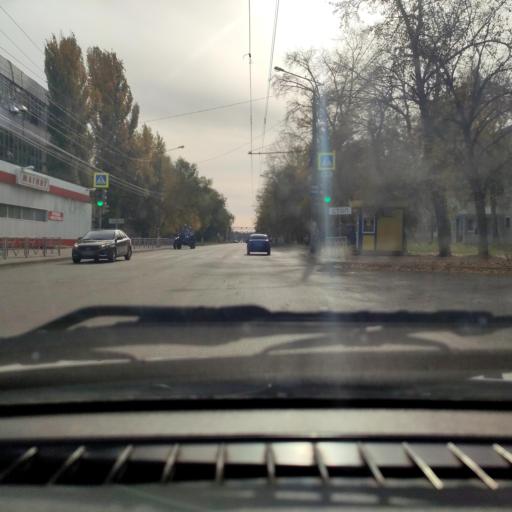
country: RU
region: Samara
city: Tol'yatti
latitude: 53.5125
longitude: 49.4297
